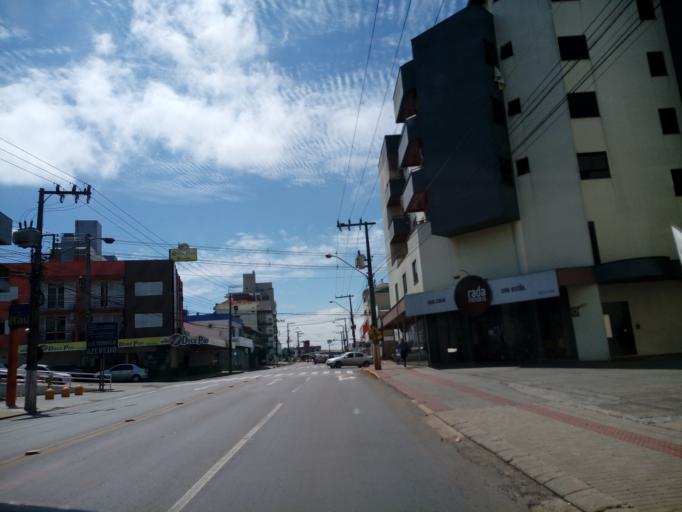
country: BR
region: Santa Catarina
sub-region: Chapeco
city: Chapeco
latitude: -27.0949
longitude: -52.6269
